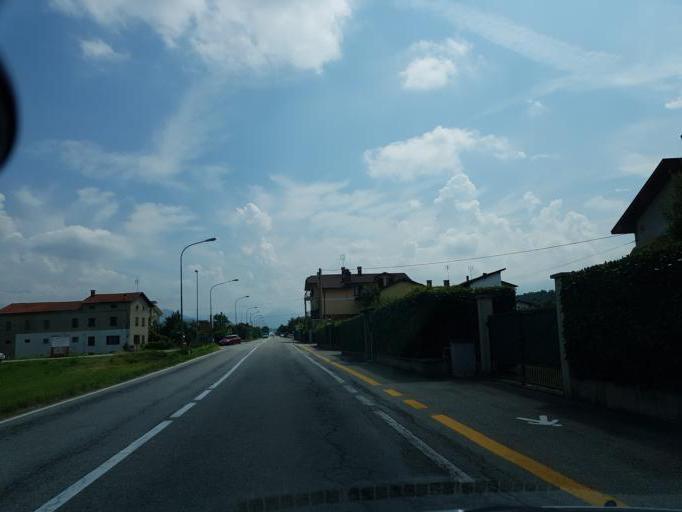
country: IT
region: Piedmont
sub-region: Provincia di Cuneo
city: Vignolo
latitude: 44.3652
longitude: 7.4743
